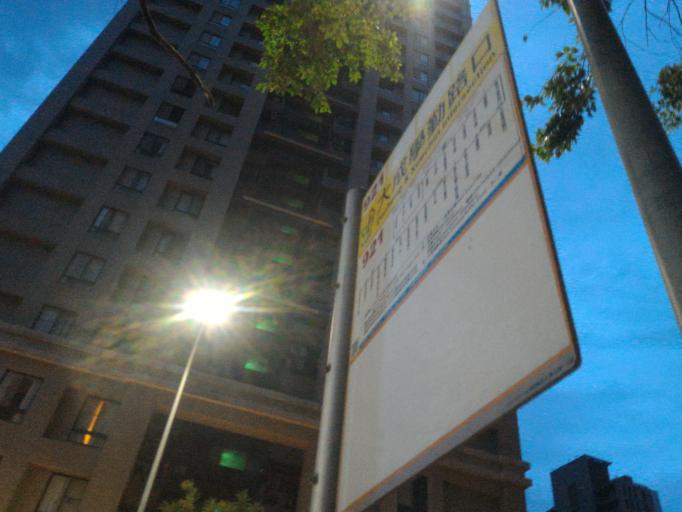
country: TW
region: Taiwan
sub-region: Taoyuan
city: Taoyuan
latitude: 24.9480
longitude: 121.3818
